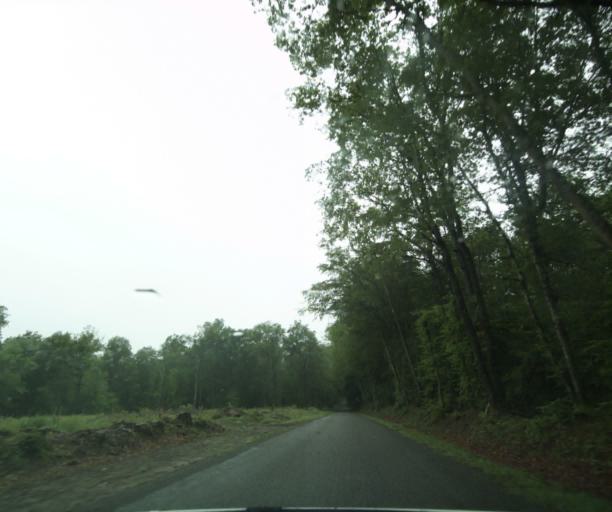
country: FR
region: Bourgogne
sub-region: Departement de Saone-et-Loire
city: Paray-le-Monial
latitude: 46.4227
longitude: 4.1901
